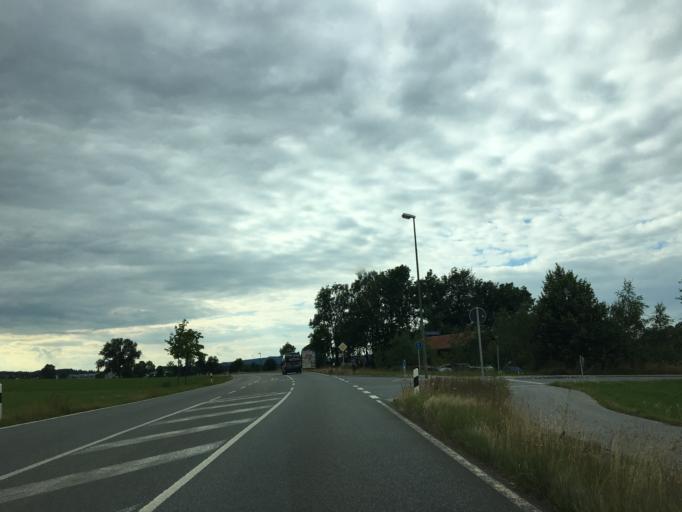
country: DE
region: Bavaria
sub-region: Upper Bavaria
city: Miesbach
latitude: 47.7877
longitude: 11.8542
